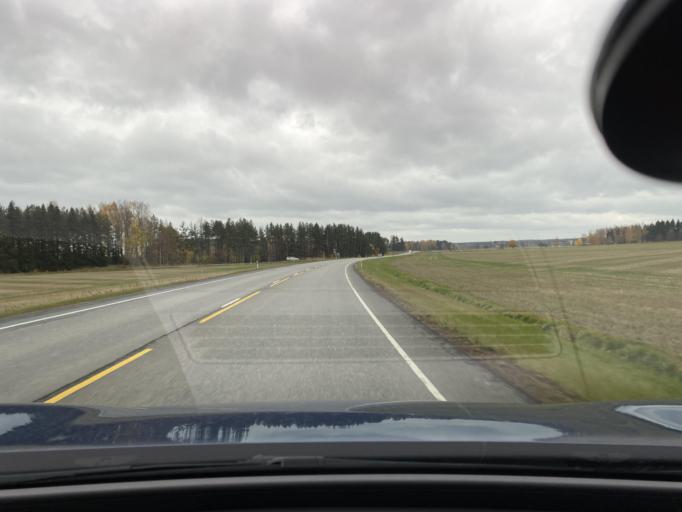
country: FI
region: Satakunta
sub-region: Rauma
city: Kiukainen
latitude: 61.1916
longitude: 22.0598
